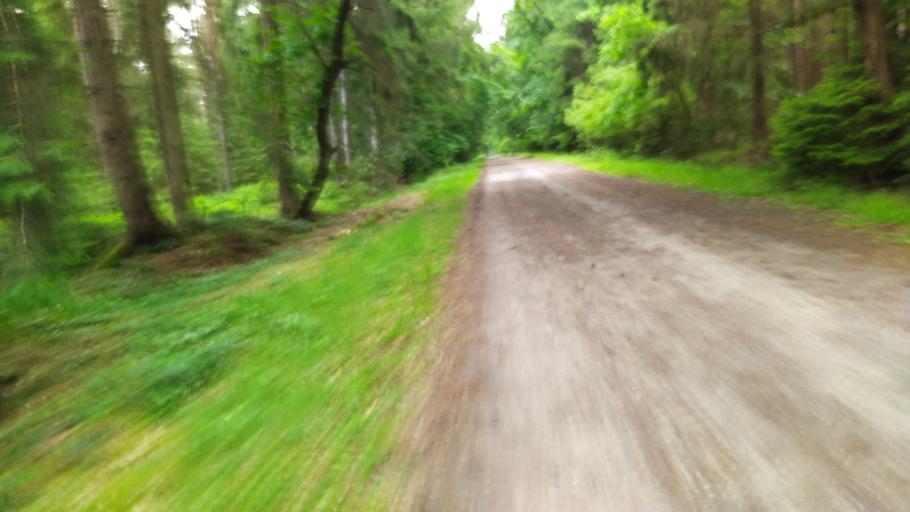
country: DE
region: Lower Saxony
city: Deinstedt
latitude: 53.4391
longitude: 9.2226
